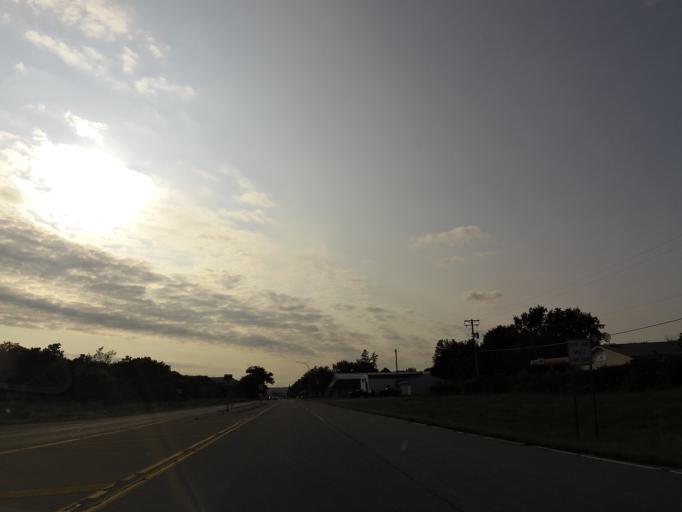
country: US
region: Minnesota
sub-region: Wabasha County
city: Lake City
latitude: 44.5096
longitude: -92.3494
